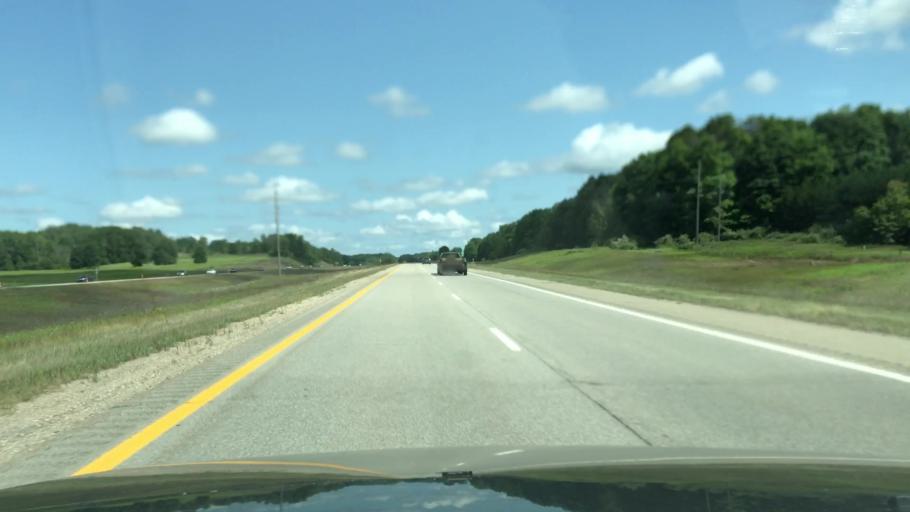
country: US
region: Michigan
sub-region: Osceola County
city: Reed City
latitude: 43.7888
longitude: -85.5341
